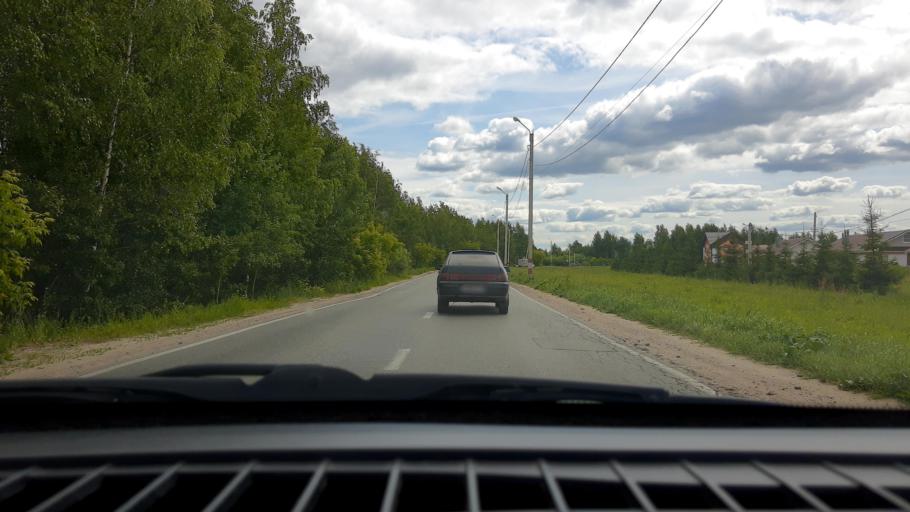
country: RU
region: Nizjnij Novgorod
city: Bor
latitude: 56.3886
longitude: 44.0417
